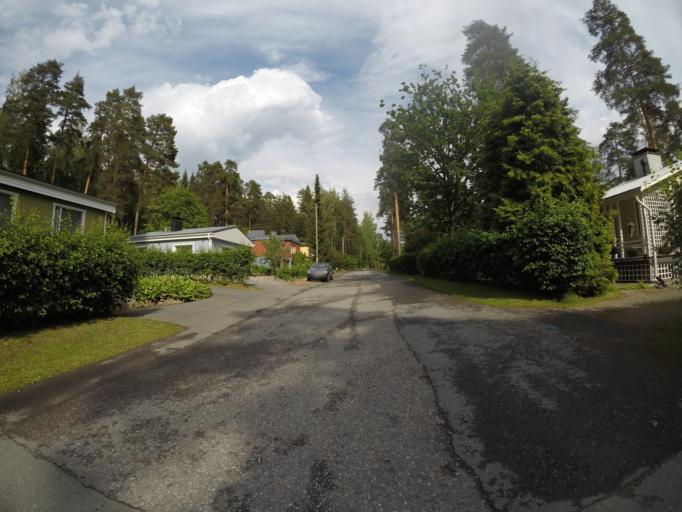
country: FI
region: Haeme
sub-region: Haemeenlinna
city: Haemeenlinna
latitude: 61.0151
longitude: 24.4699
